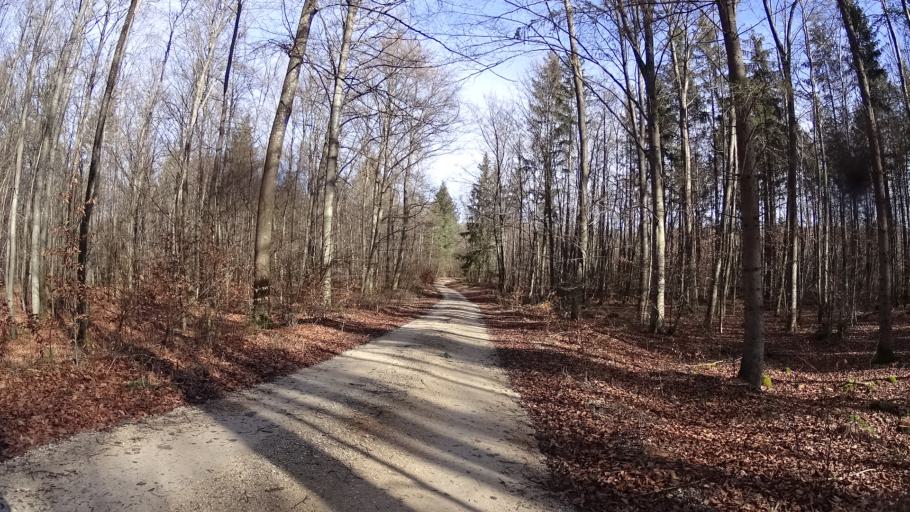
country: DE
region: Bavaria
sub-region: Upper Bavaria
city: Walting
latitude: 48.8998
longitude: 11.3282
